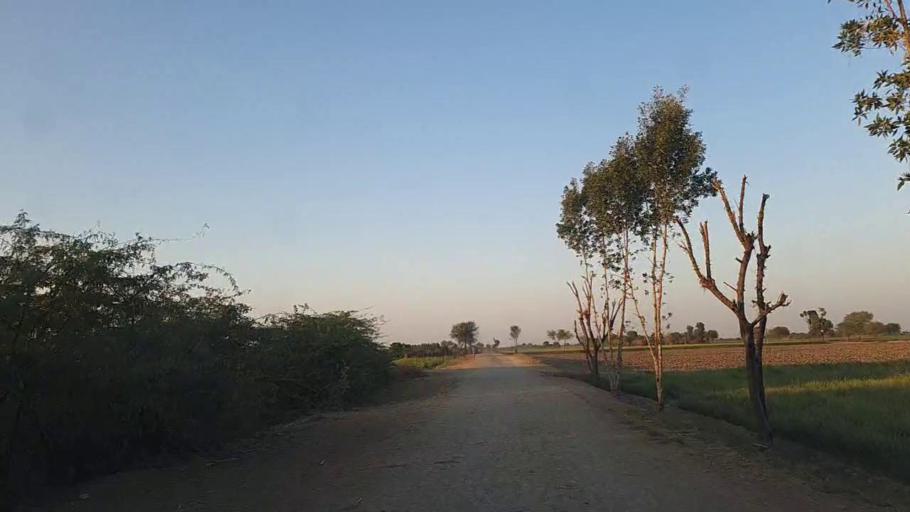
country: PK
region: Sindh
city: Naukot
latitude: 25.0399
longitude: 69.4099
